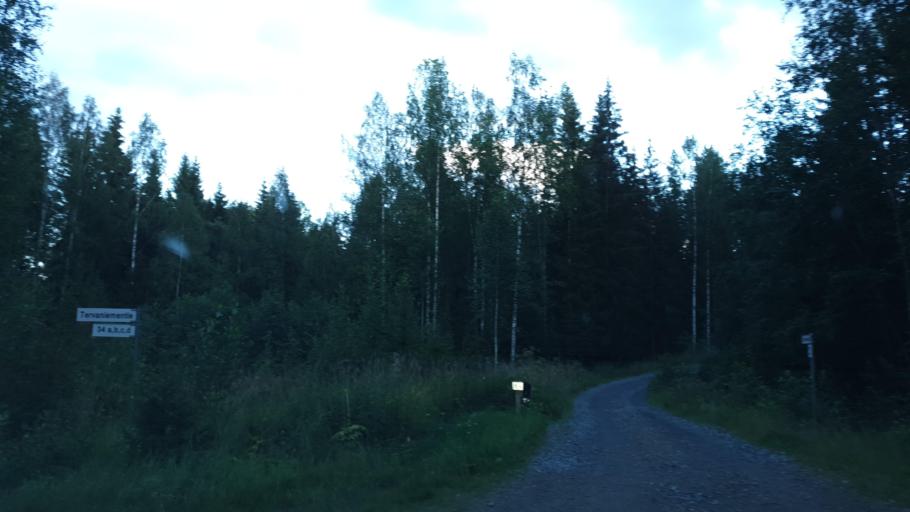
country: FI
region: Northern Savo
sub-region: Varkaus
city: Leppaevirta
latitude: 62.5809
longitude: 27.6254
